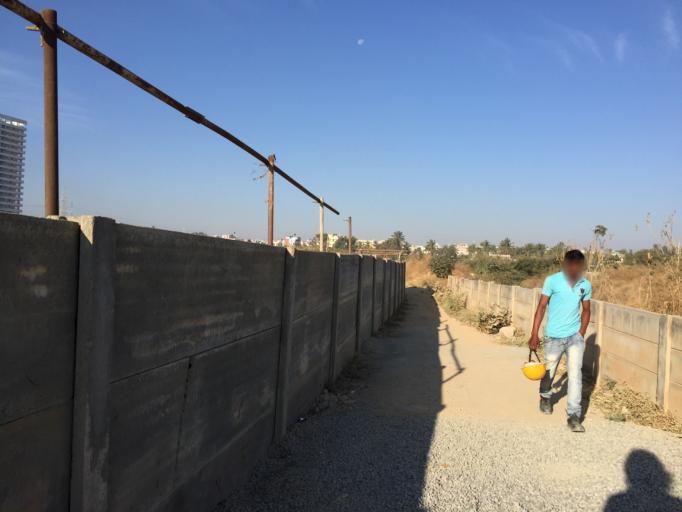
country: IN
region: Karnataka
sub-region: Bangalore Urban
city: Yelahanka
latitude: 13.0542
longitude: 77.6190
